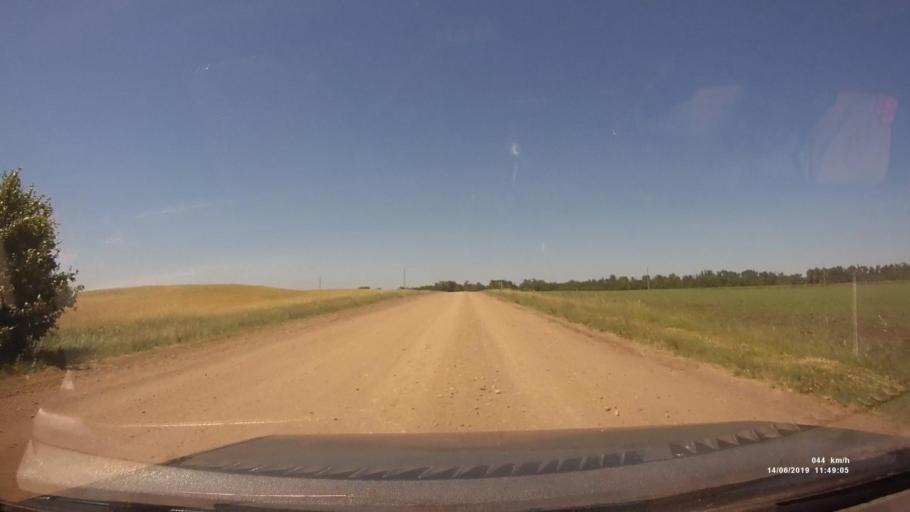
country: RU
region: Rostov
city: Kazanskaya
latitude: 49.8526
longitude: 41.2810
